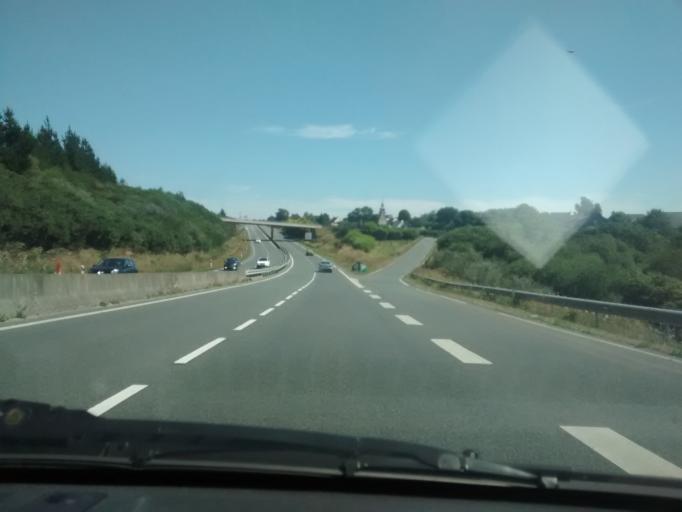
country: FR
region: Brittany
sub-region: Departement des Cotes-d'Armor
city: Rospez
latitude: 48.7193
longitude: -3.4165
